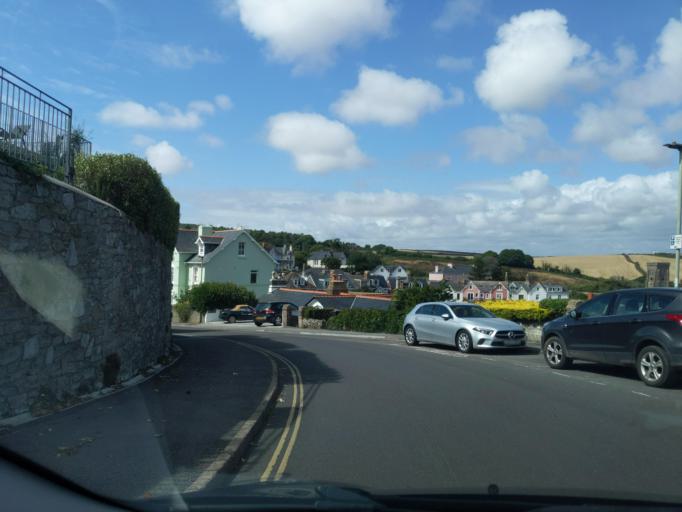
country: GB
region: England
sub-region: Devon
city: Salcombe
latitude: 50.2368
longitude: -3.7680
